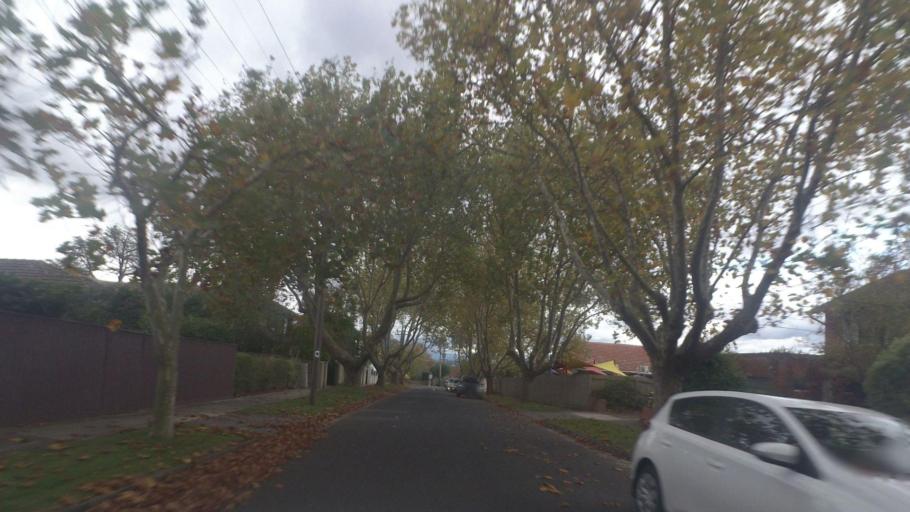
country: AU
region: Victoria
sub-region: Whitehorse
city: Surrey Hills
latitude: -37.8284
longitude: 145.1104
